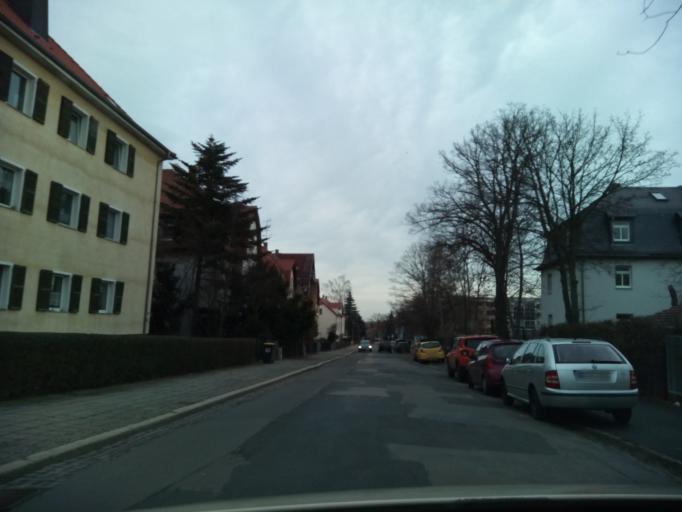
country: DE
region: Saxony
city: Freiberg
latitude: 50.9067
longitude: 13.3313
